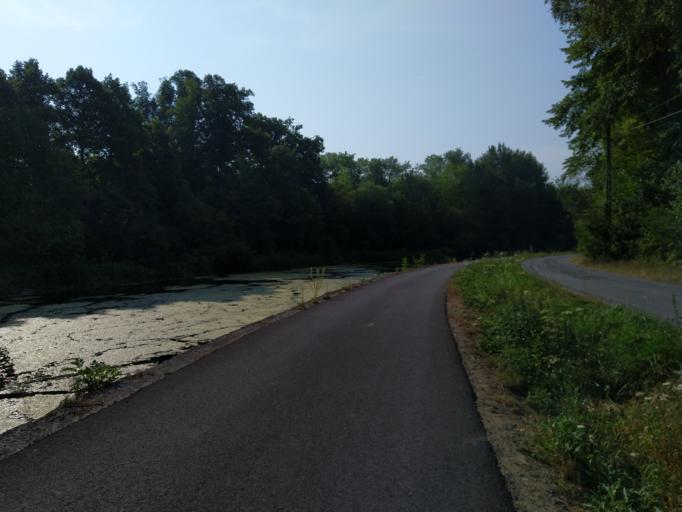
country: BE
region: Wallonia
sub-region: Province du Hainaut
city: Seneffe
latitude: 50.5797
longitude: 4.2529
